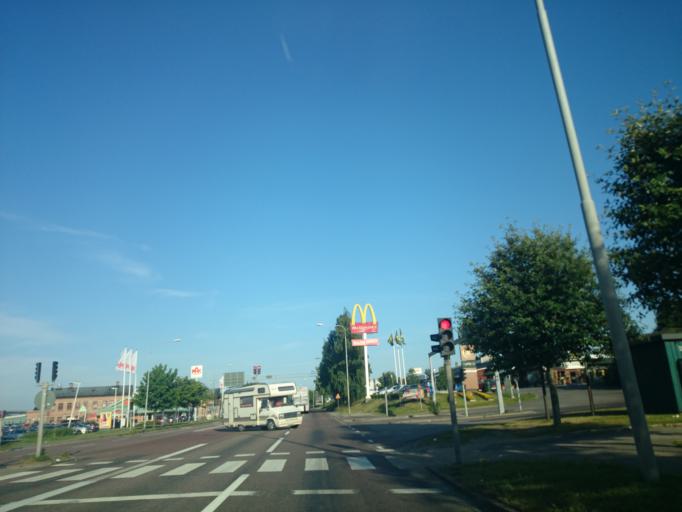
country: SE
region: Vaesternorrland
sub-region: Sundsvalls Kommun
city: Sundsvall
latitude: 62.3872
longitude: 17.3169
